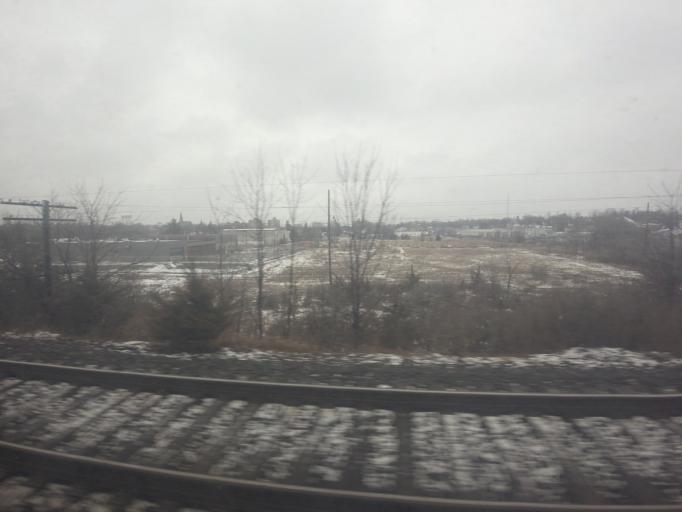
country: CA
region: Ontario
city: Belleville
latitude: 44.1728
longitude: -77.3932
